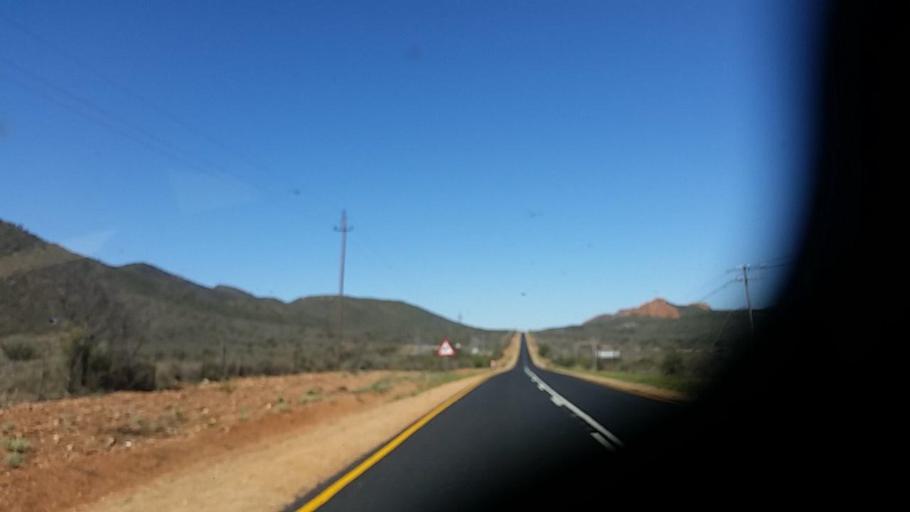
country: ZA
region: Western Cape
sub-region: Eden District Municipality
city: Oudtshoorn
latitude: -33.4859
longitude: 22.5660
